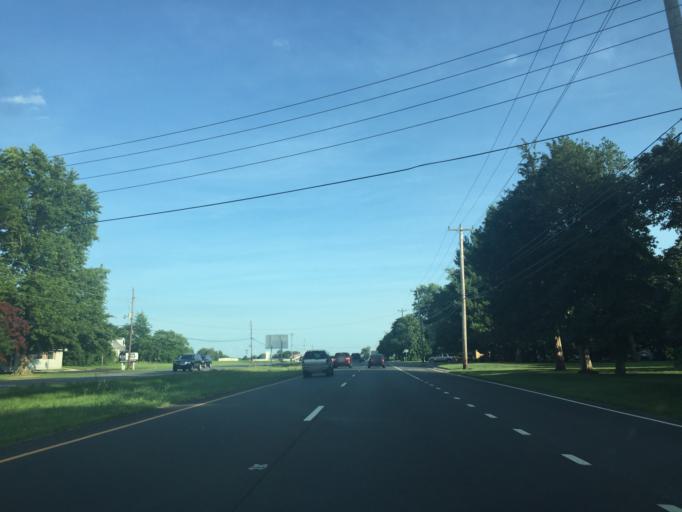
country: US
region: Delaware
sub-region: Kent County
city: Smyrna
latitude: 39.2749
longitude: -75.5909
